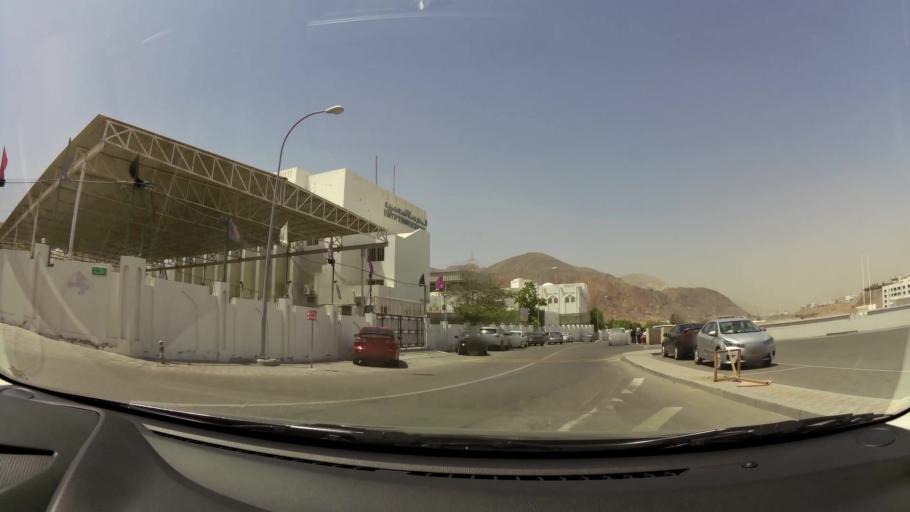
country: OM
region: Muhafazat Masqat
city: Bawshar
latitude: 23.5861
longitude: 58.4484
